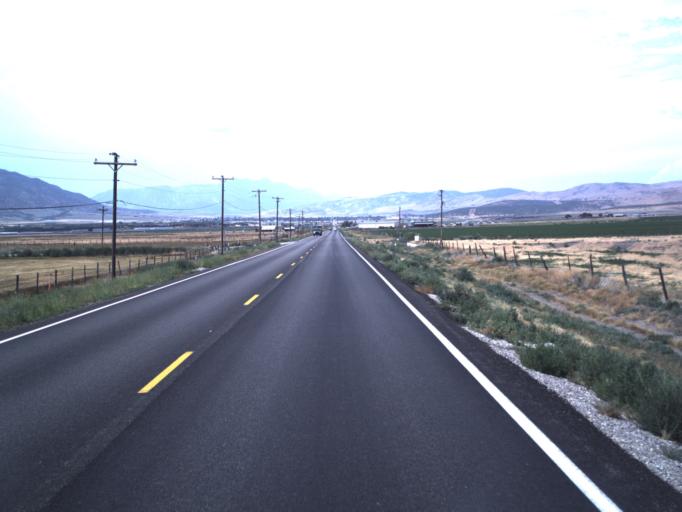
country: US
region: Utah
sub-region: Sanpete County
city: Moroni
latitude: 39.5665
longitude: -111.6051
